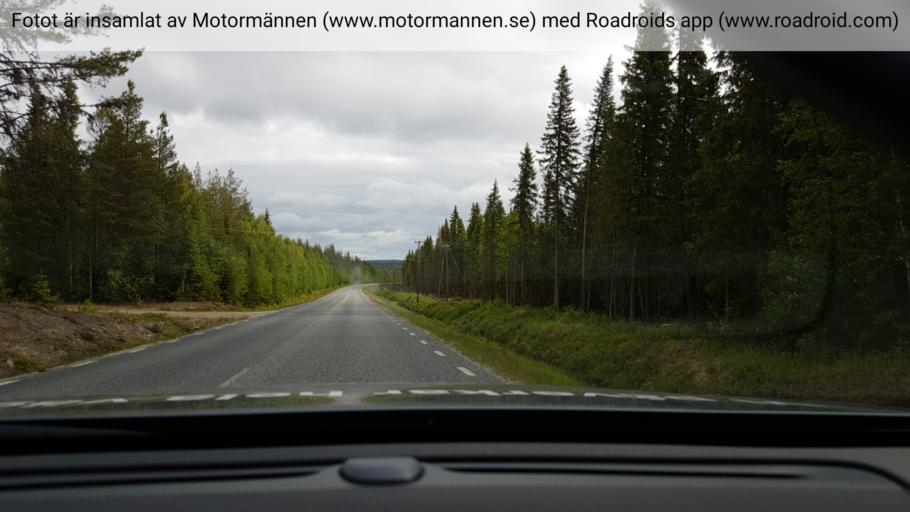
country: SE
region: Vaesterbotten
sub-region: Asele Kommun
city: Insjon
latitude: 64.2668
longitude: 17.5705
